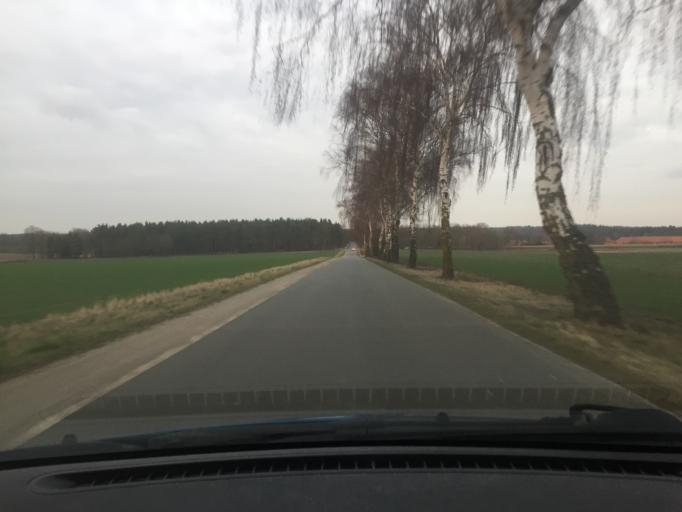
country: DE
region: Lower Saxony
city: Jelmstorf
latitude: 53.1051
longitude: 10.5345
